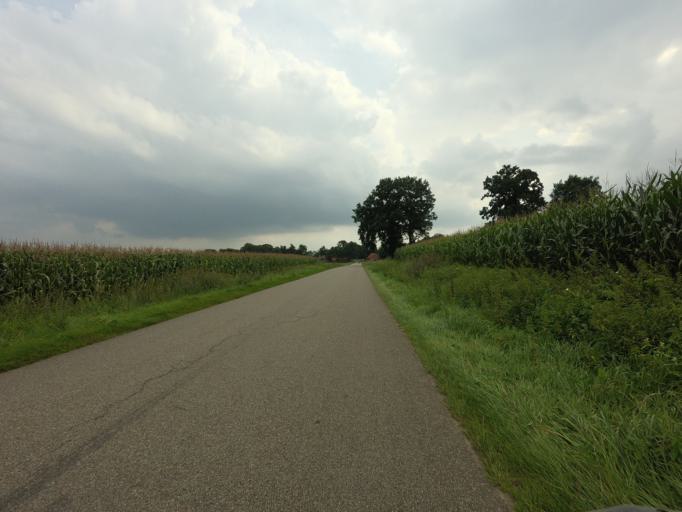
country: DE
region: Lower Saxony
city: Uelsen
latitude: 52.4582
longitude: 6.9144
